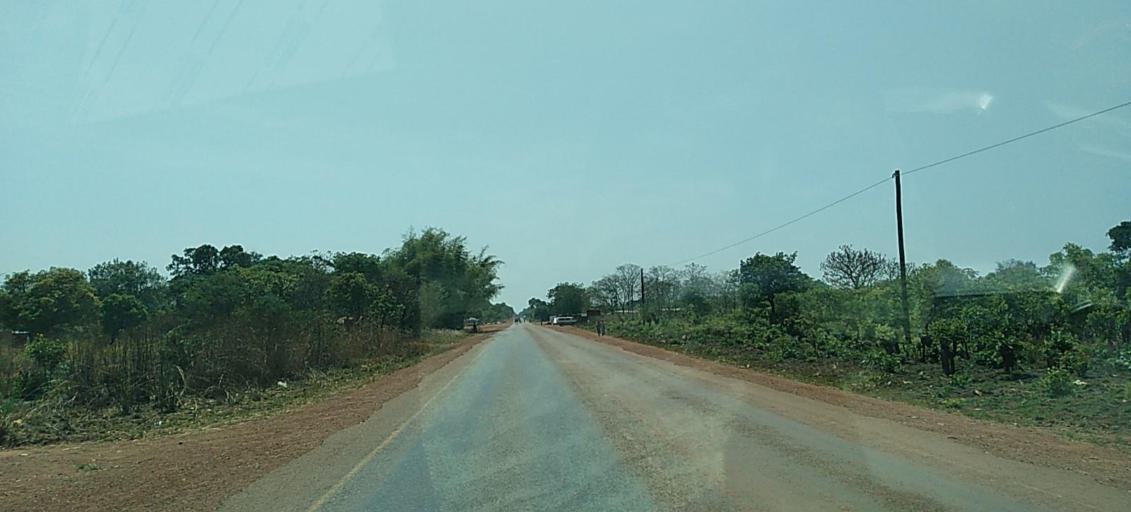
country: ZM
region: North-Western
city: Solwezi
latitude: -12.3613
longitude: 25.9388
